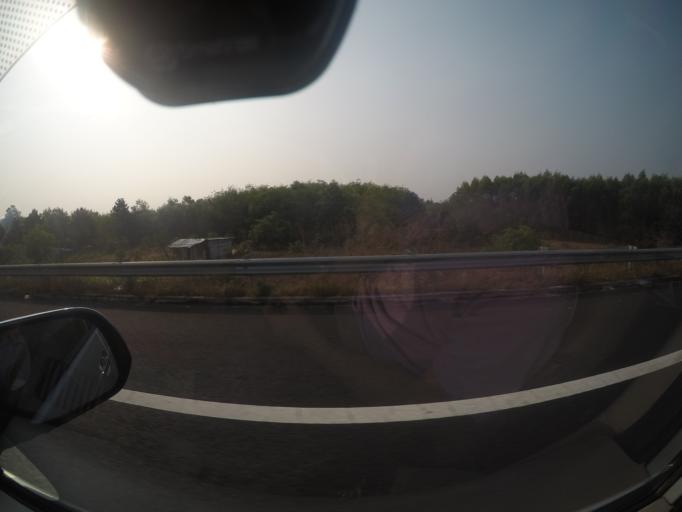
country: VN
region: Dong Nai
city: Thong Nhat
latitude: 10.9038
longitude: 107.1529
